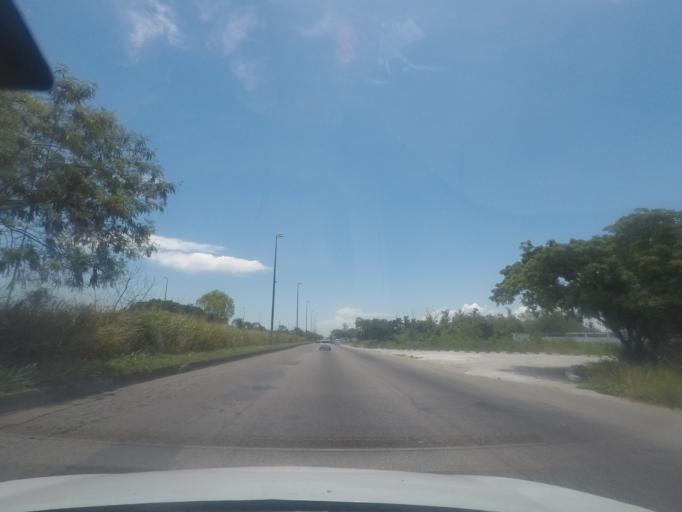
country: BR
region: Rio de Janeiro
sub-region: Itaguai
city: Itaguai
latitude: -22.8894
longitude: -43.6622
